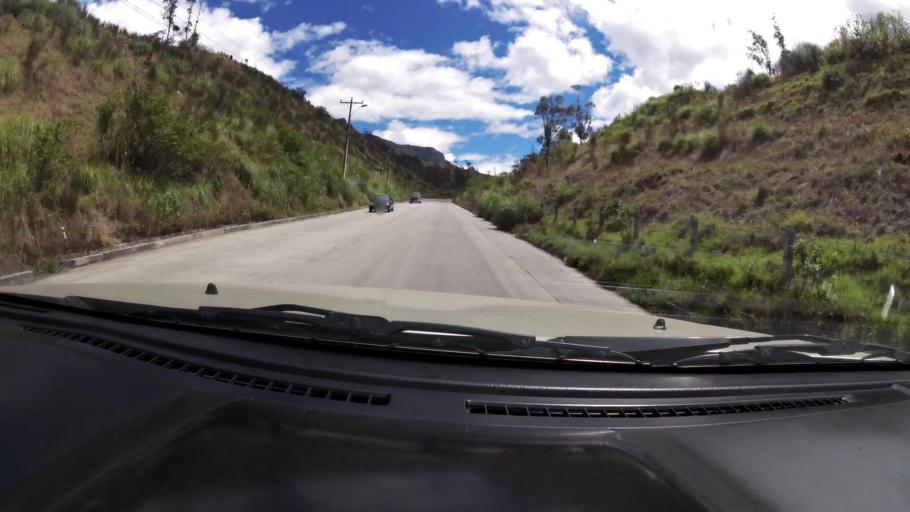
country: EC
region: Azuay
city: Cuenca
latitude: -3.1495
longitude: -79.1466
